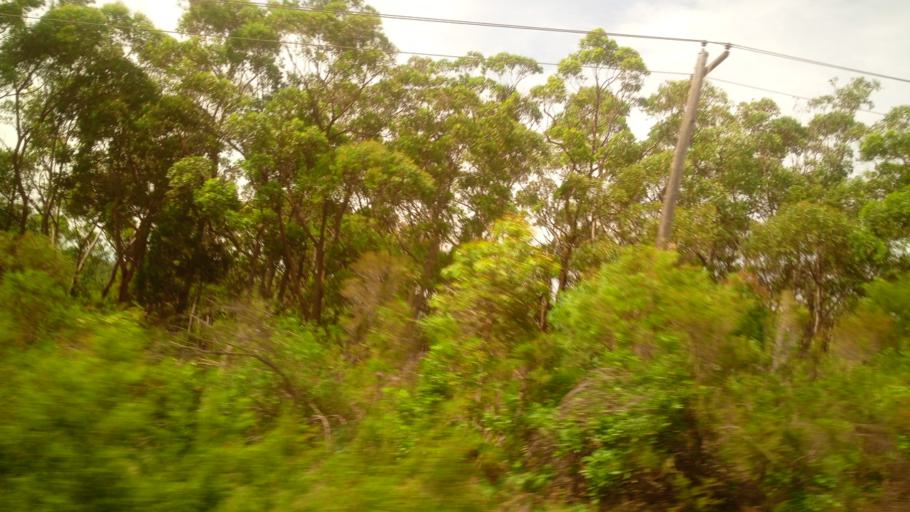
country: AU
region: New South Wales
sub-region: Blue Mountains Municipality
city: Hazelbrook
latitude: -33.7131
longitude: 150.5192
